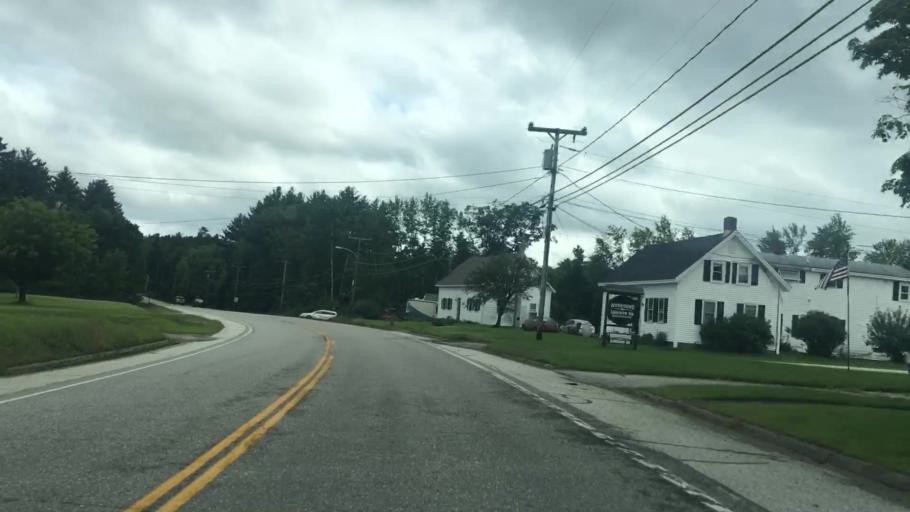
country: US
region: Maine
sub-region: York County
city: Lake Arrowhead
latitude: 43.6510
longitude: -70.7609
